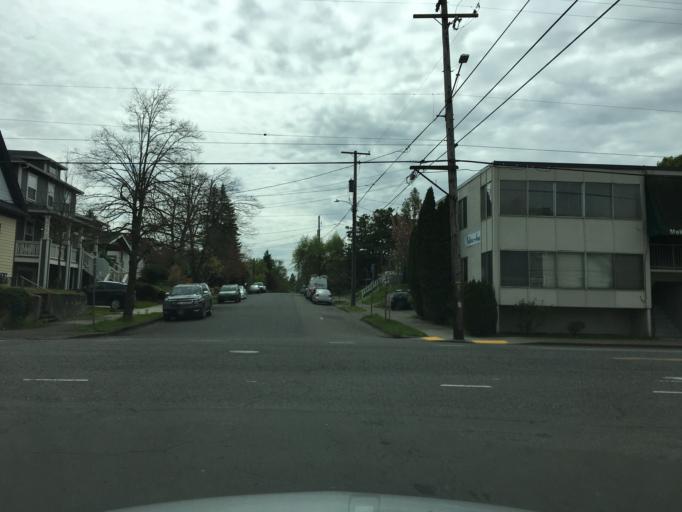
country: US
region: Oregon
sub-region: Multnomah County
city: Lents
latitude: 45.5230
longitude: -122.5836
